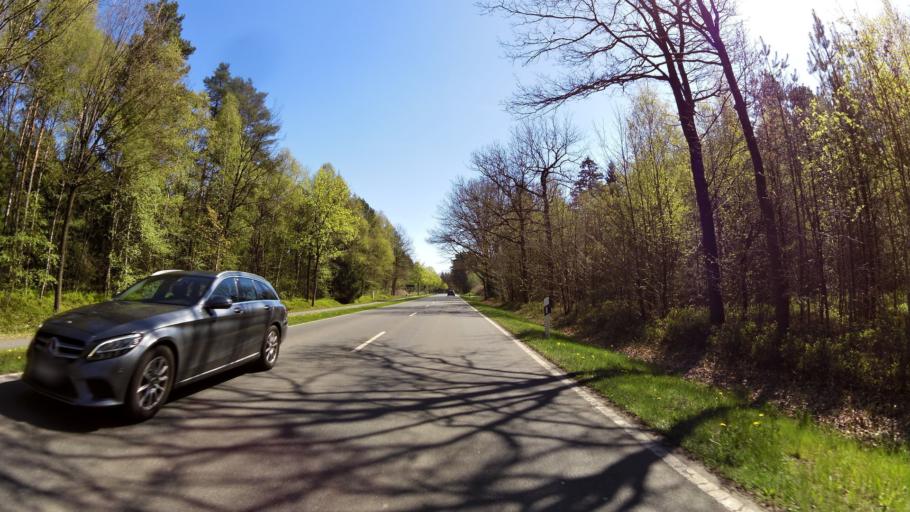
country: DE
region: Lower Saxony
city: Soltau
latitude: 53.0090
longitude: 9.7960
